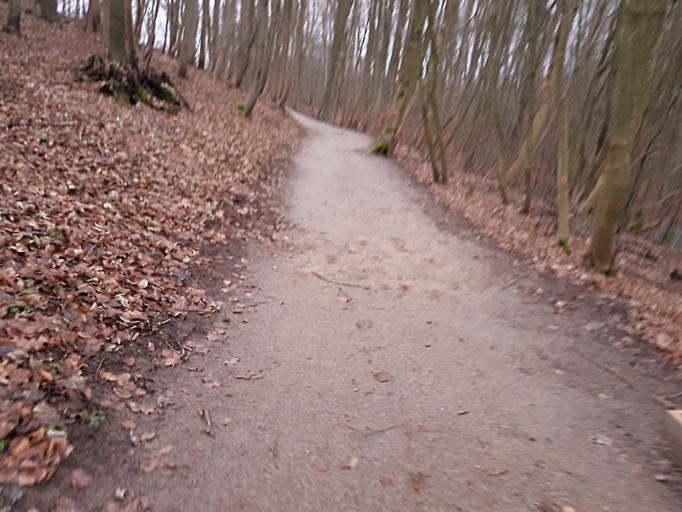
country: DE
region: Mecklenburg-Vorpommern
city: Ostseebad Binz
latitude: 54.3802
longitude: 13.6287
